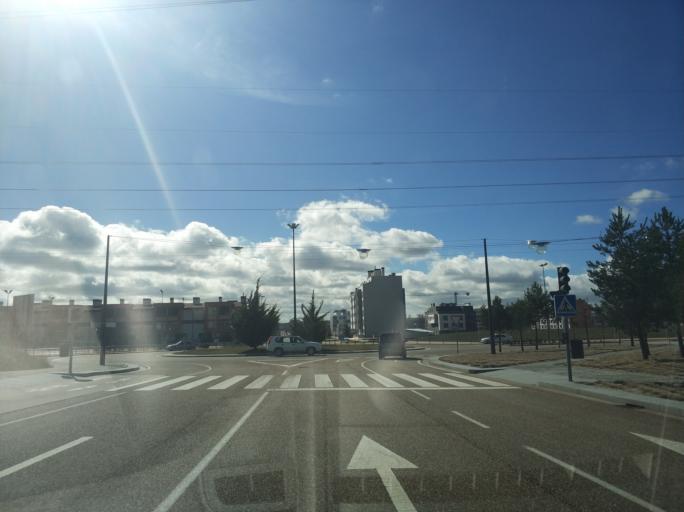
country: ES
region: Castille and Leon
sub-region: Provincia de Burgos
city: Burgos
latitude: 42.3701
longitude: -3.6631
